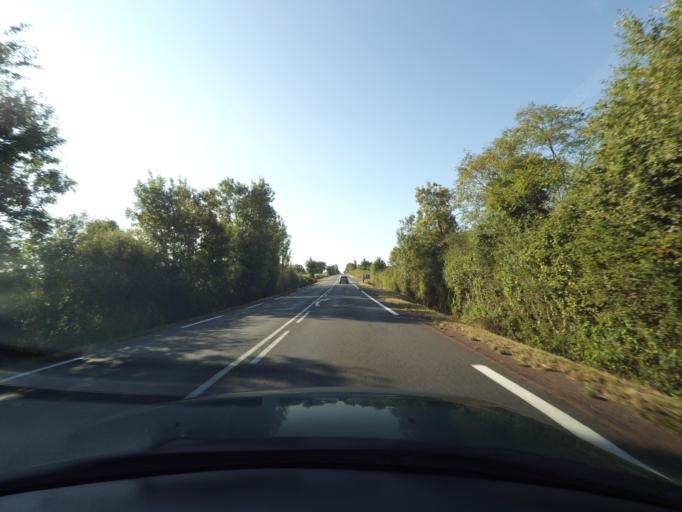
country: FR
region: Poitou-Charentes
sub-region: Departement des Deux-Sevres
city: Viennay
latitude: 46.6802
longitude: -0.2640
